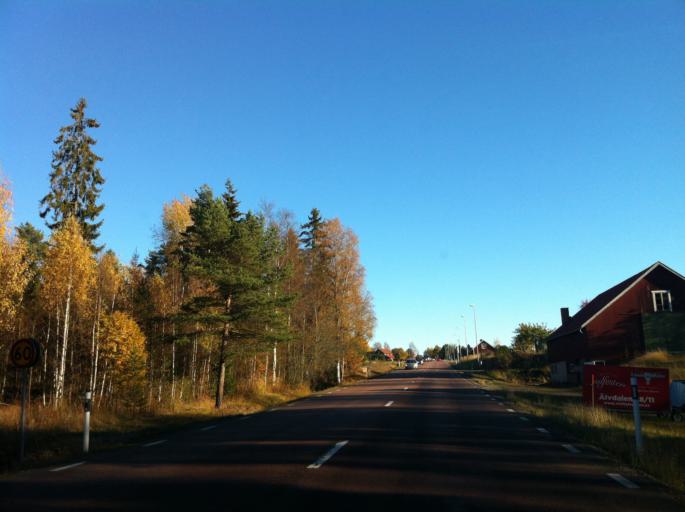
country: SE
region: Dalarna
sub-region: Leksand Municipality
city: Siljansnas
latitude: 60.9266
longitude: 14.8069
